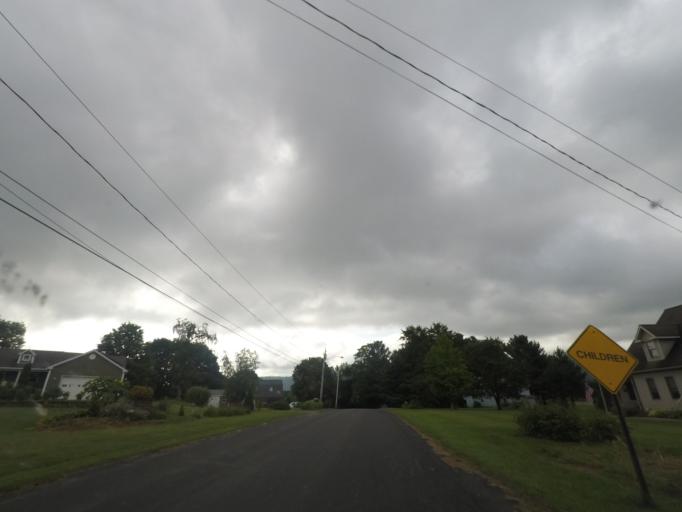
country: US
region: Massachusetts
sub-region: Berkshire County
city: Richmond
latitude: 42.4258
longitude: -73.3158
